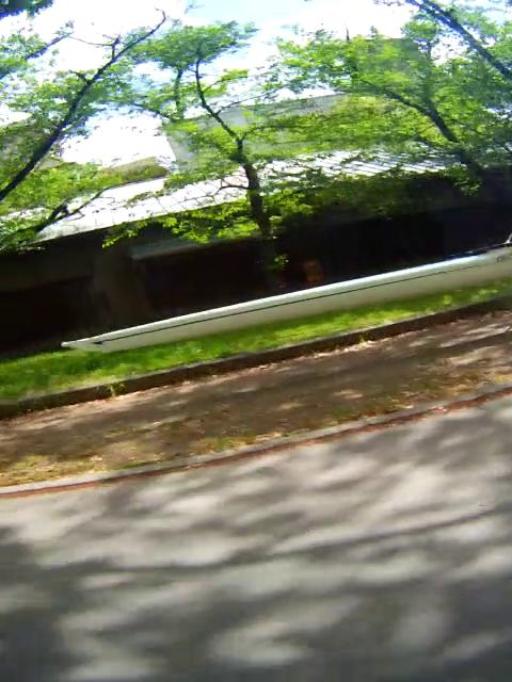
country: JP
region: Osaka
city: Osaka-shi
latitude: 34.7048
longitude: 135.5195
